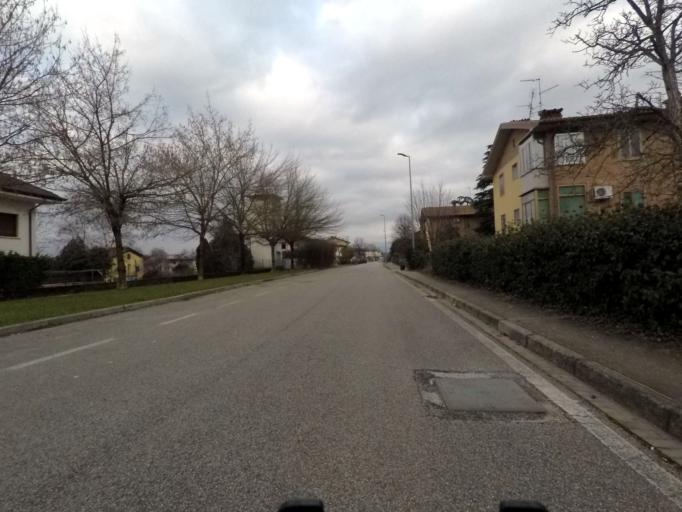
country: IT
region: Friuli Venezia Giulia
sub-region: Provincia di Udine
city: Tavagnacco
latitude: 46.1141
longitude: 13.2113
